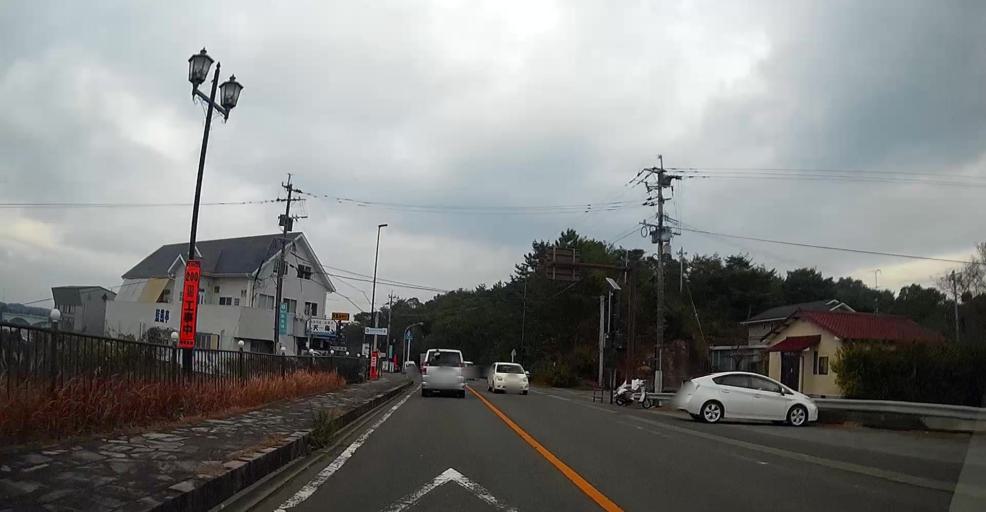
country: JP
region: Kumamoto
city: Yatsushiro
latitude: 32.5242
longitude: 130.4237
